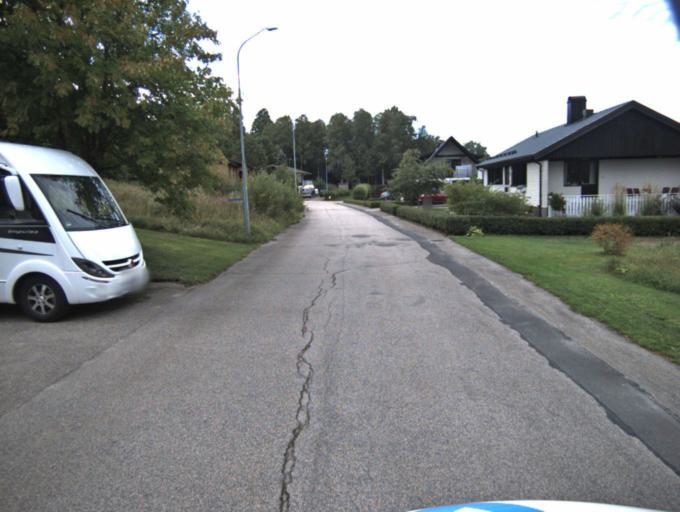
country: SE
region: Vaestra Goetaland
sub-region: Ulricehamns Kommun
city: Ulricehamn
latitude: 57.8613
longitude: 13.4195
